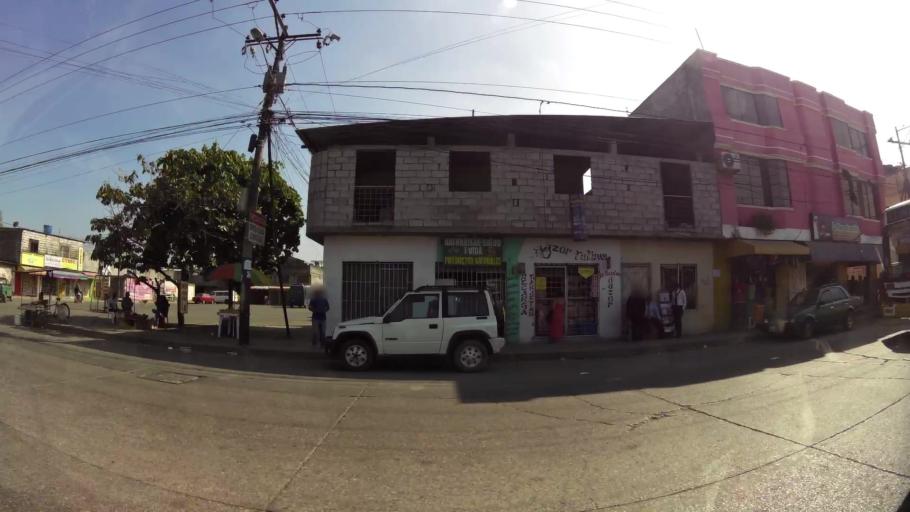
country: EC
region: Guayas
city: Eloy Alfaro
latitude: -2.1691
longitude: -79.8038
